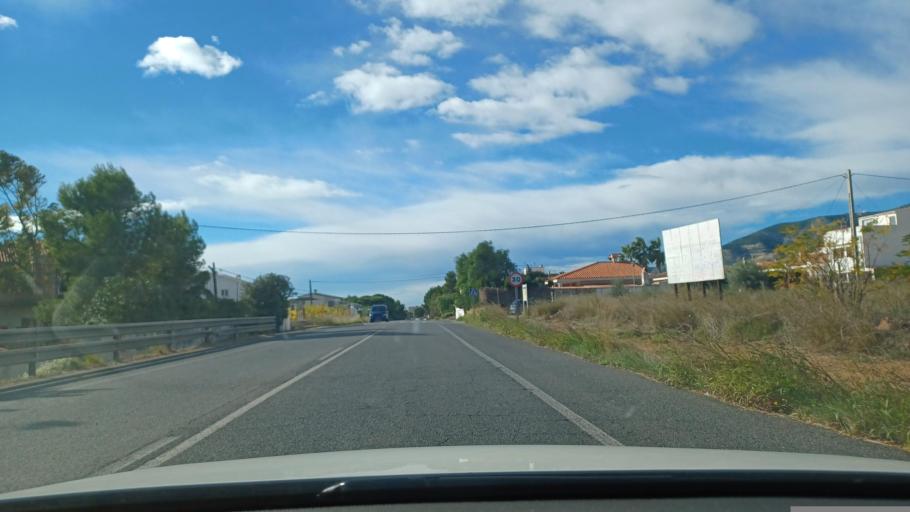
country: ES
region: Catalonia
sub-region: Provincia de Tarragona
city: Sant Carles de la Rapita
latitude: 40.6009
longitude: 0.5764
